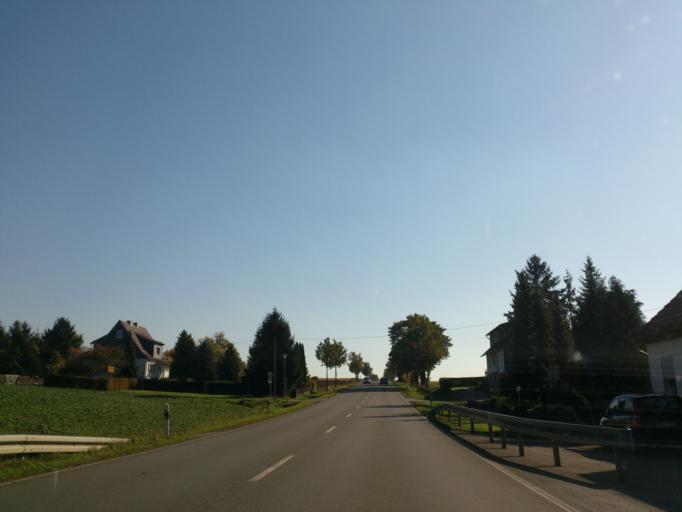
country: DE
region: Hesse
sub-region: Regierungsbezirk Kassel
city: Breuna
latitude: 51.4677
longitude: 9.1980
